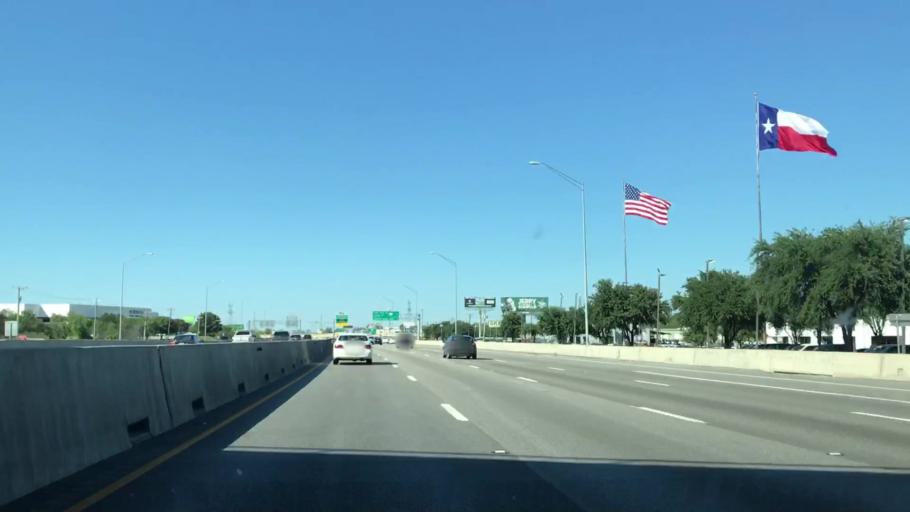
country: US
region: Texas
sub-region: Denton County
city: Lewisville
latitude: 33.0562
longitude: -97.0115
